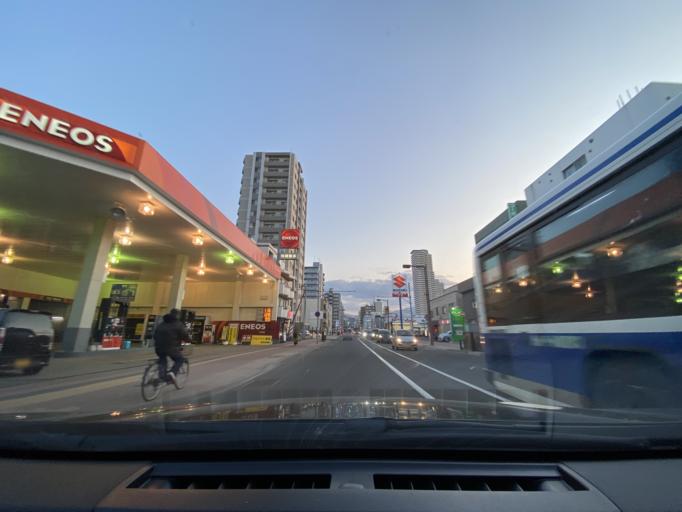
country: JP
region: Hokkaido
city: Sapporo
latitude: 43.0846
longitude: 141.3126
